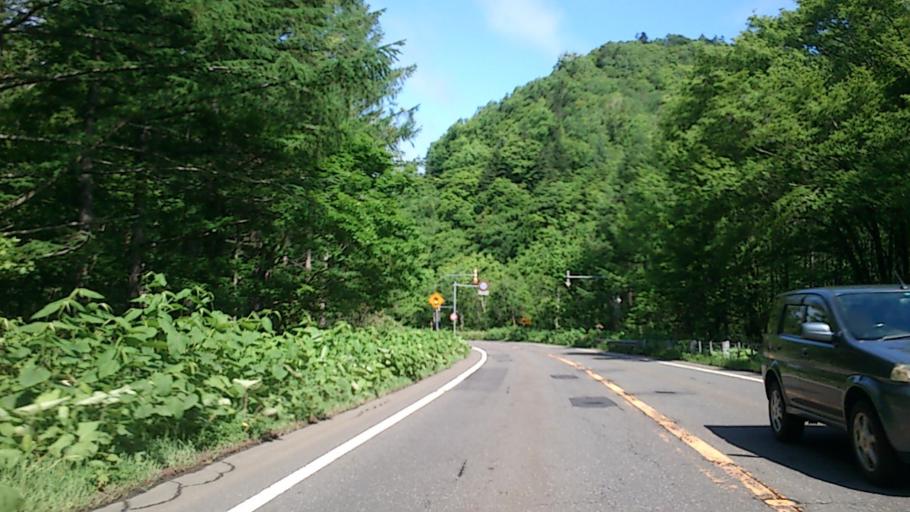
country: JP
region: Hokkaido
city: Shiraoi
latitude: 42.7166
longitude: 141.2250
